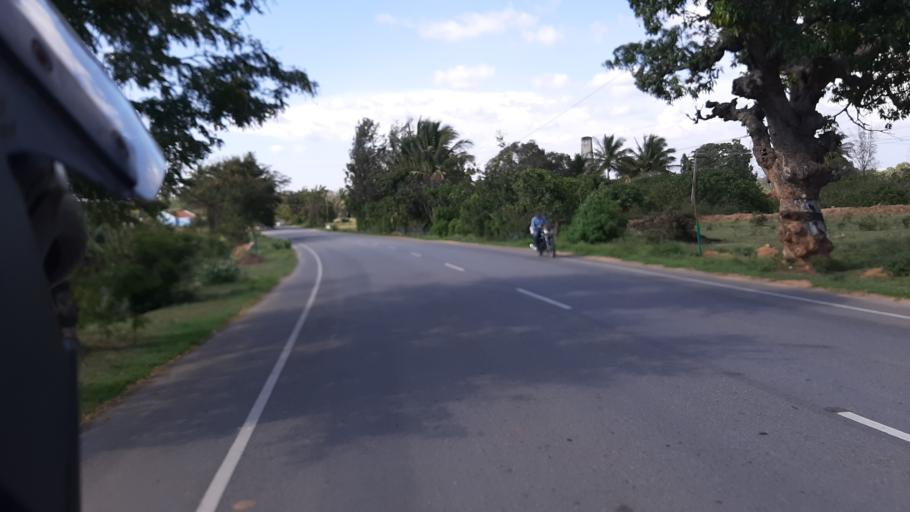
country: IN
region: Tamil Nadu
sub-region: Krishnagiri
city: Denkanikota
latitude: 12.5412
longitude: 77.7889
